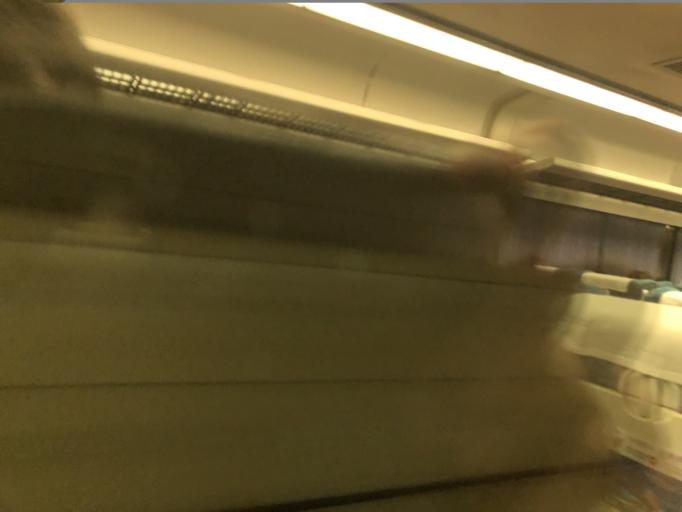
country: JP
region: Kochi
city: Nakamura
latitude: 33.0627
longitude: 133.1052
